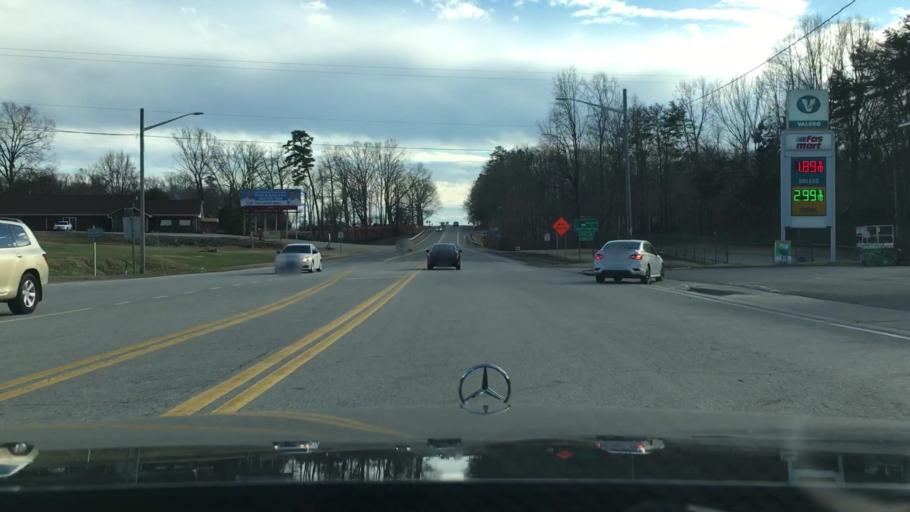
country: US
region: Virginia
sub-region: City of Danville
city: Danville
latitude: 36.5420
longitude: -79.4009
